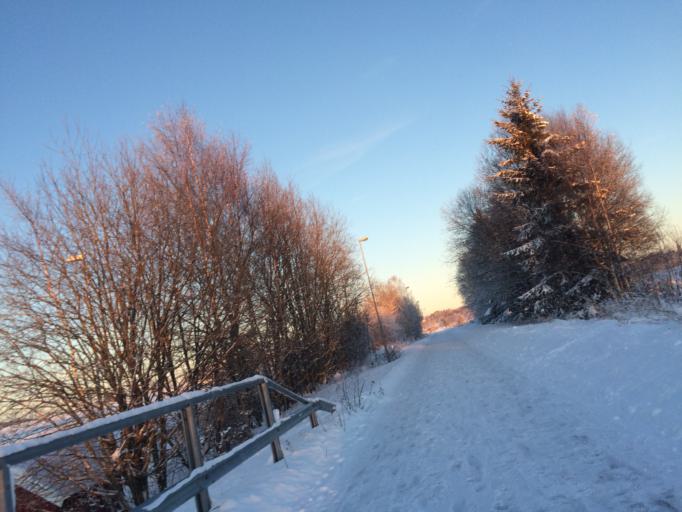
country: NO
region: Akershus
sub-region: Ski
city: Ski
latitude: 59.6914
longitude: 10.8218
